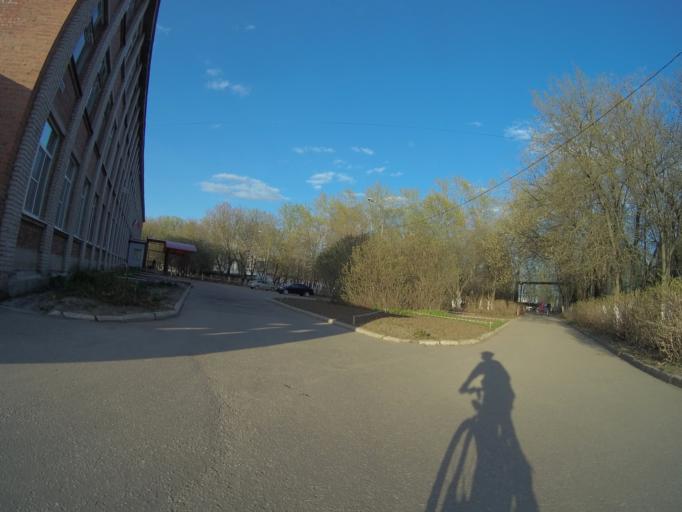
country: RU
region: Vladimir
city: Vladimir
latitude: 56.1446
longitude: 40.3670
